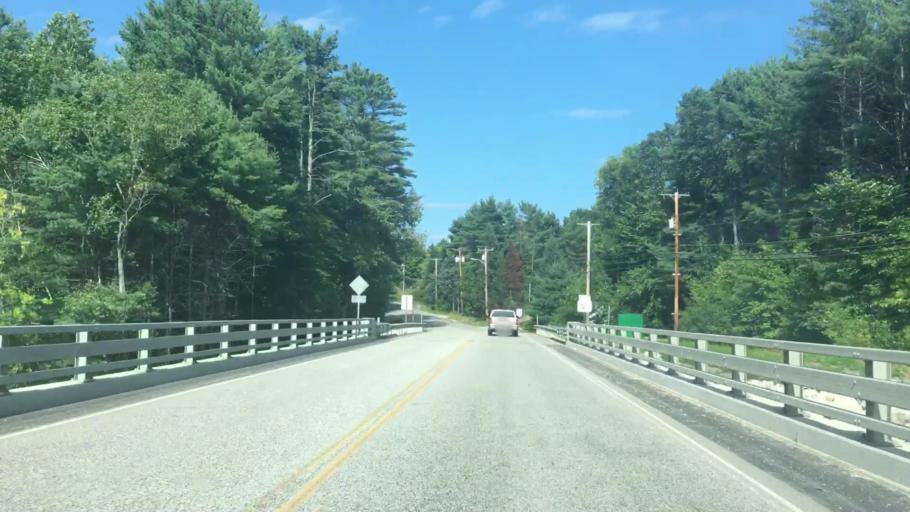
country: US
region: Maine
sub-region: Oxford County
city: Oxford
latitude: 44.1369
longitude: -70.4901
